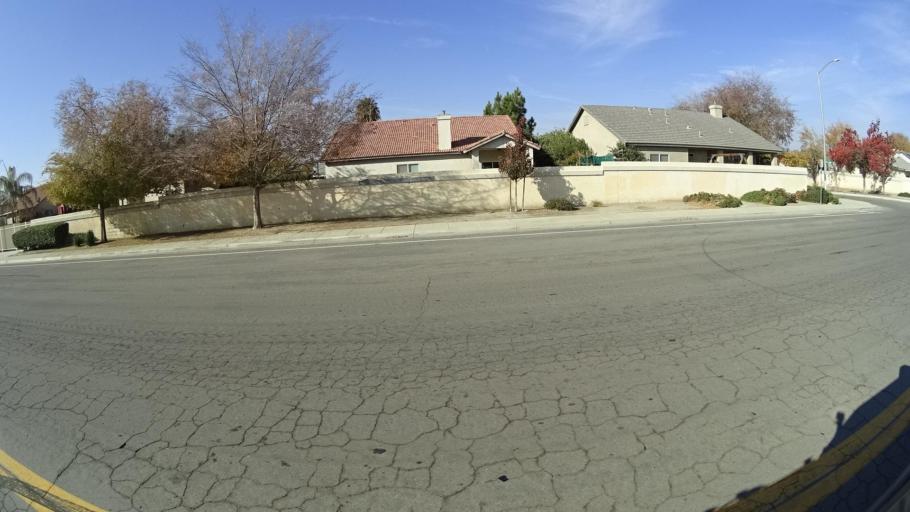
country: US
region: California
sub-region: Kern County
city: Lamont
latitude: 35.3593
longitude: -118.8964
